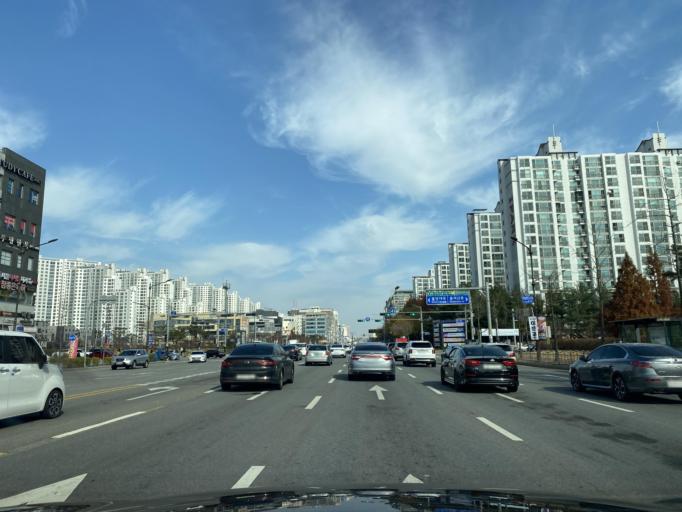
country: KR
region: Chungcheongnam-do
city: Cheonan
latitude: 36.8067
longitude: 127.1070
